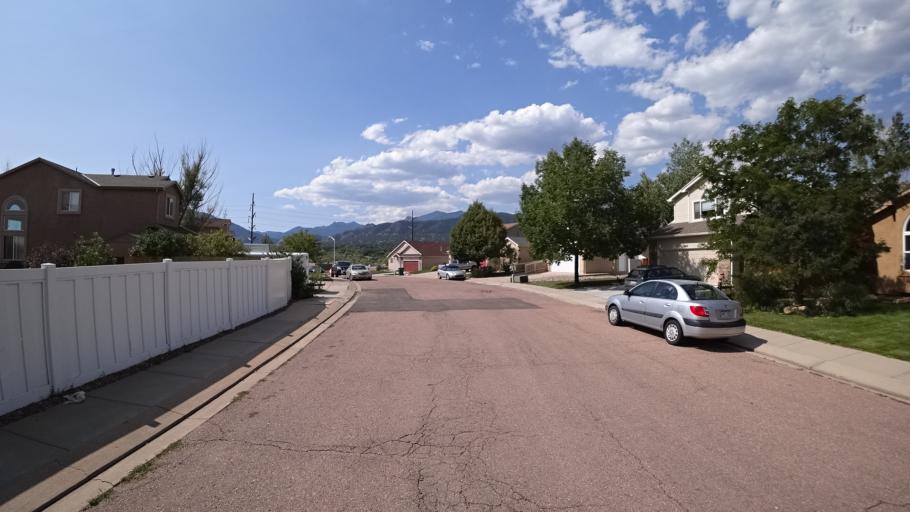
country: US
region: Colorado
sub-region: El Paso County
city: Colorado Springs
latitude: 38.8254
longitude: -104.8520
